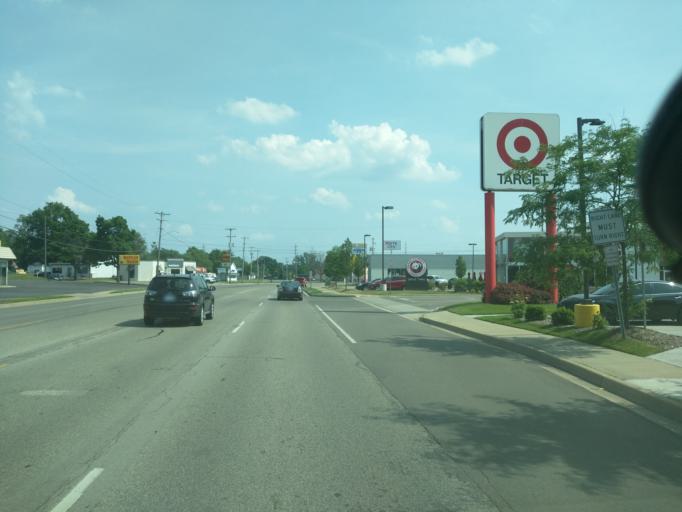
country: US
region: Michigan
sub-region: Jackson County
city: Jackson
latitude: 42.2678
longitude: -84.4241
